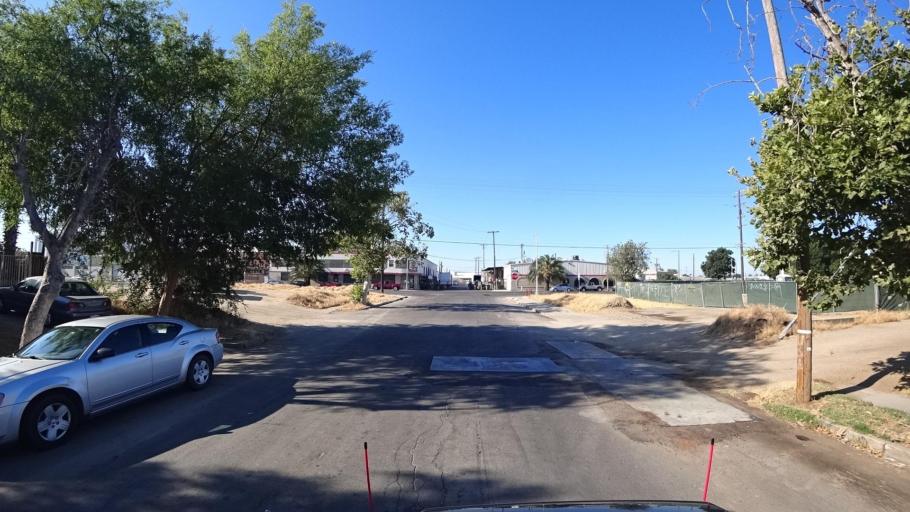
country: US
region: California
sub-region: Fresno County
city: Fresno
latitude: 36.7509
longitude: -119.8108
